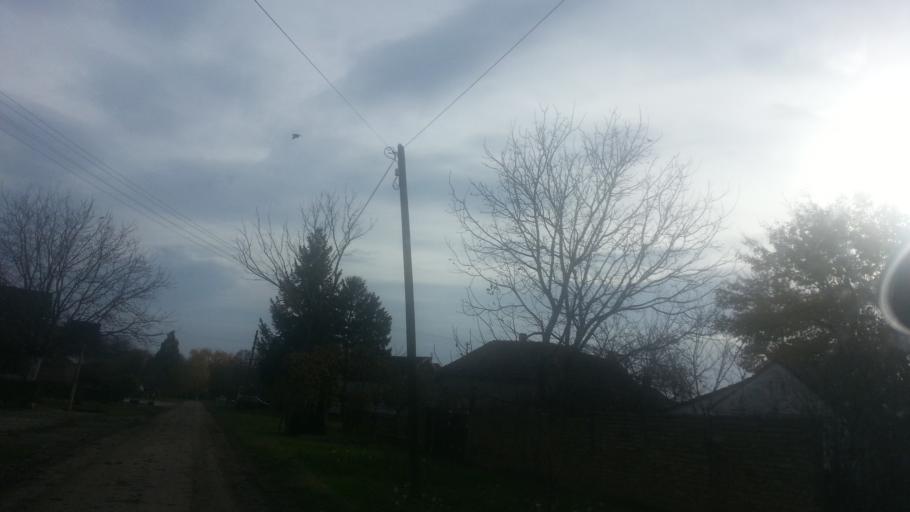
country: RS
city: Putinci
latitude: 44.9990
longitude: 19.9776
